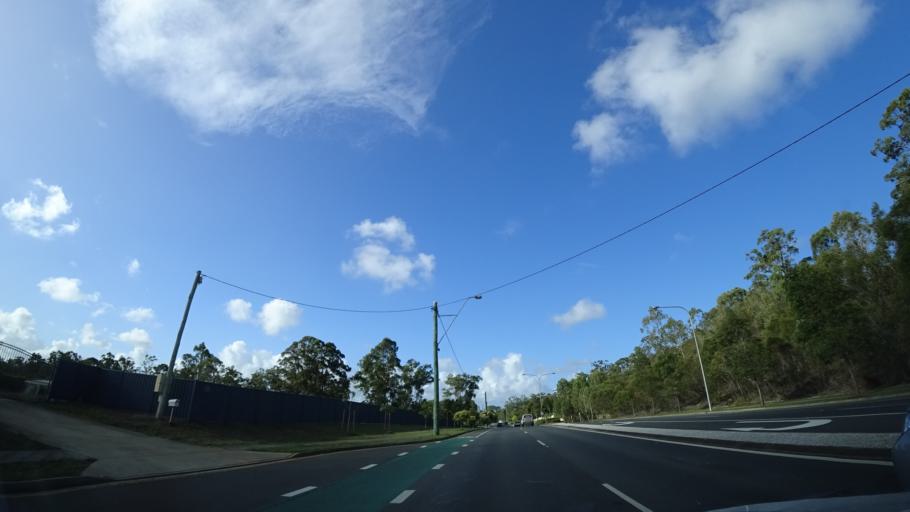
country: AU
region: Queensland
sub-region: Brisbane
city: Bridegman Downs
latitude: -27.3417
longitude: 152.9976
